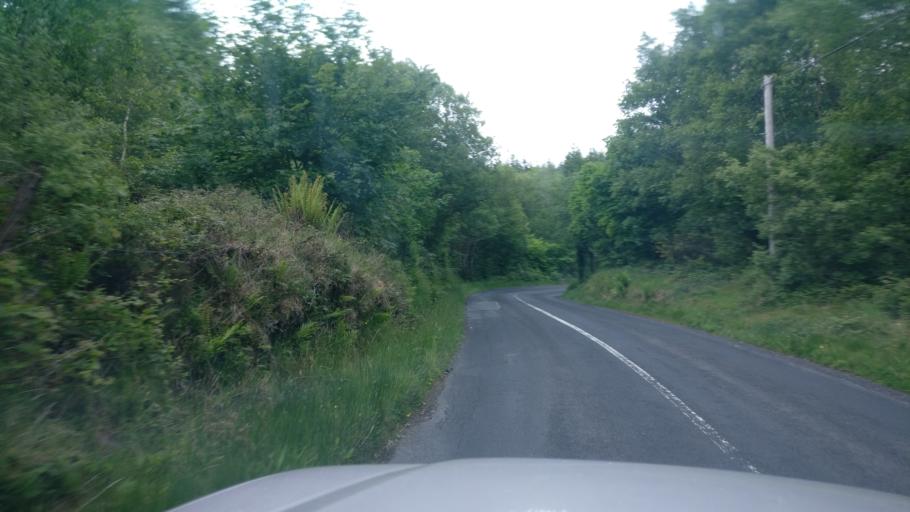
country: IE
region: Connaught
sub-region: County Galway
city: Gort
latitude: 53.0569
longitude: -8.6613
